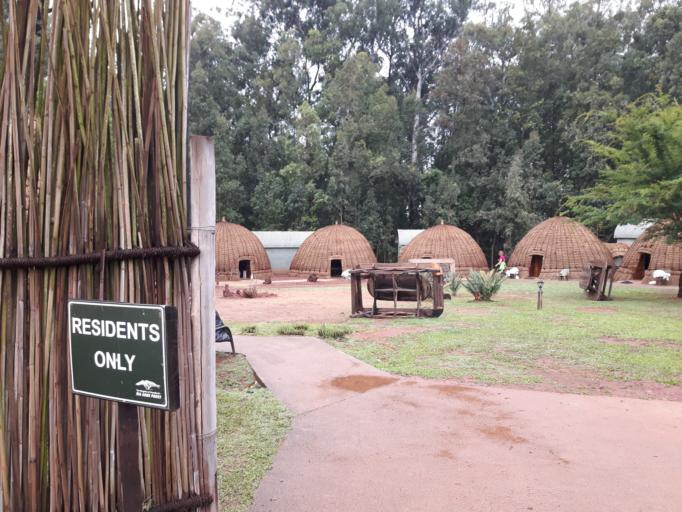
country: SZ
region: Hhohho
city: Lobamba
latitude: -26.4925
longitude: 31.1860
